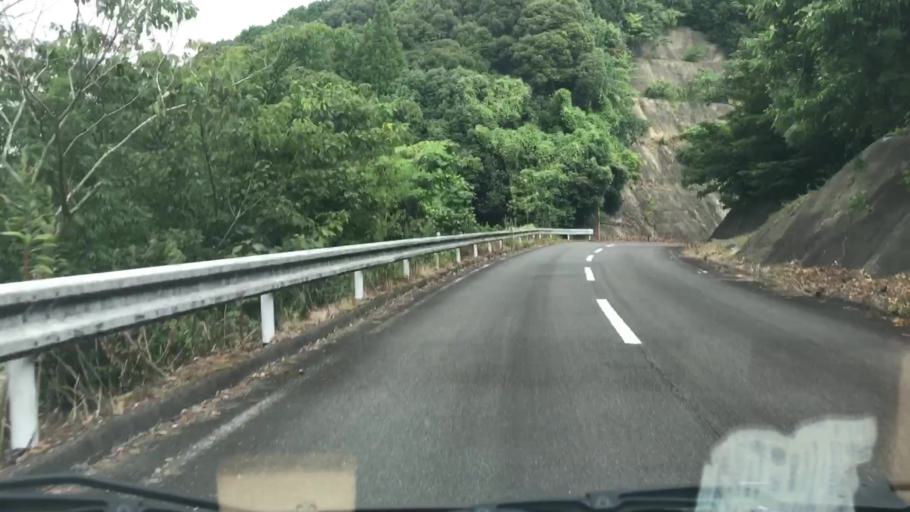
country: JP
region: Saga Prefecture
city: Takeocho-takeo
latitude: 33.2274
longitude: 129.9772
